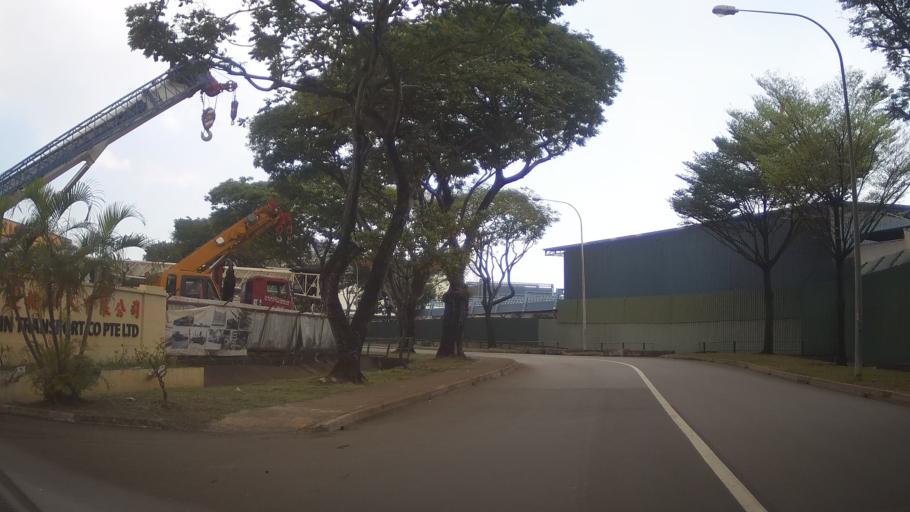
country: SG
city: Singapore
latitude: 1.3033
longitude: 103.6763
